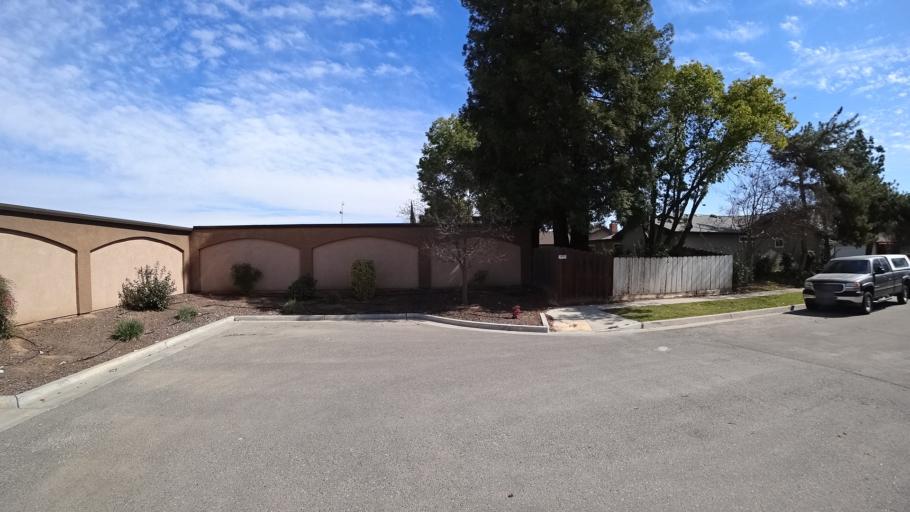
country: US
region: California
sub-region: Fresno County
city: Fresno
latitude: 36.8461
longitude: -119.8129
